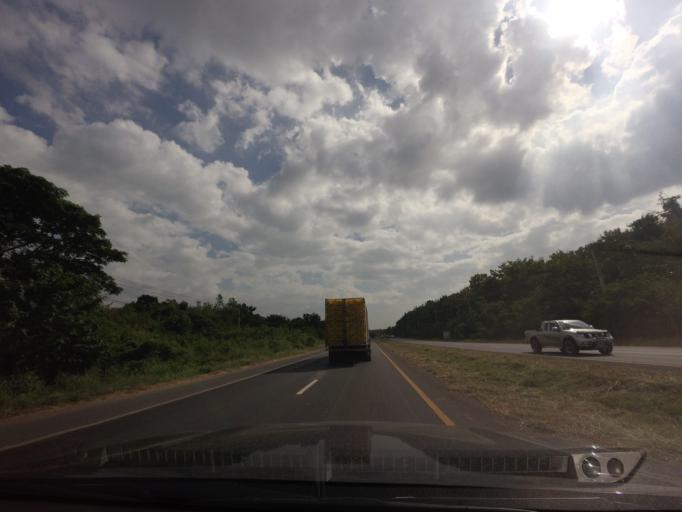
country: TH
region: Lop Buri
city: Chai Badan
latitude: 15.2879
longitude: 101.1266
